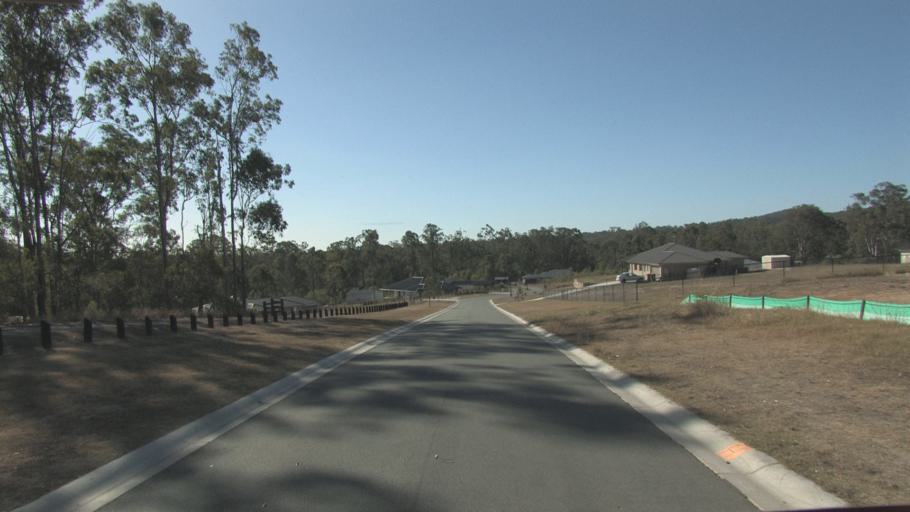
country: AU
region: Queensland
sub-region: Logan
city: Cedar Vale
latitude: -27.8651
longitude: 153.0535
